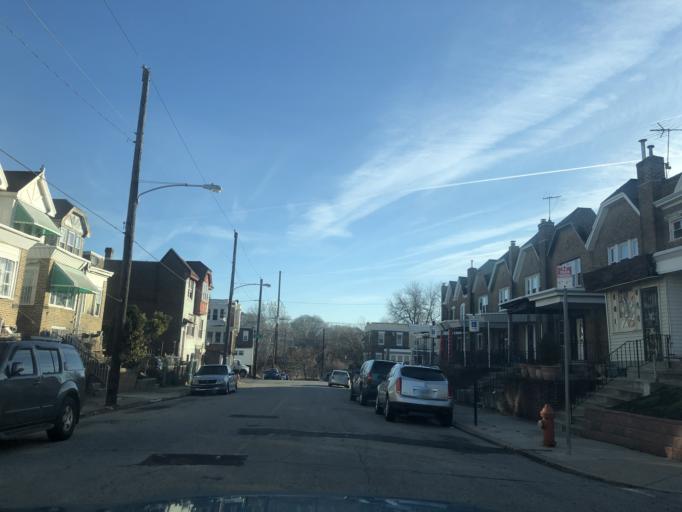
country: US
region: Pennsylvania
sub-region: Montgomery County
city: Bala-Cynwyd
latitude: 39.9827
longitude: -75.2297
